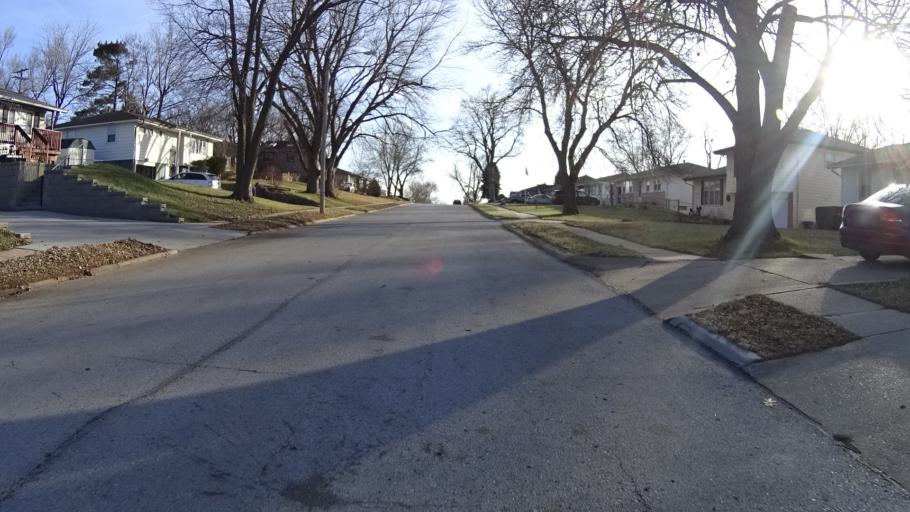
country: US
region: Nebraska
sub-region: Sarpy County
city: La Vista
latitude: 41.1897
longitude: -95.9969
